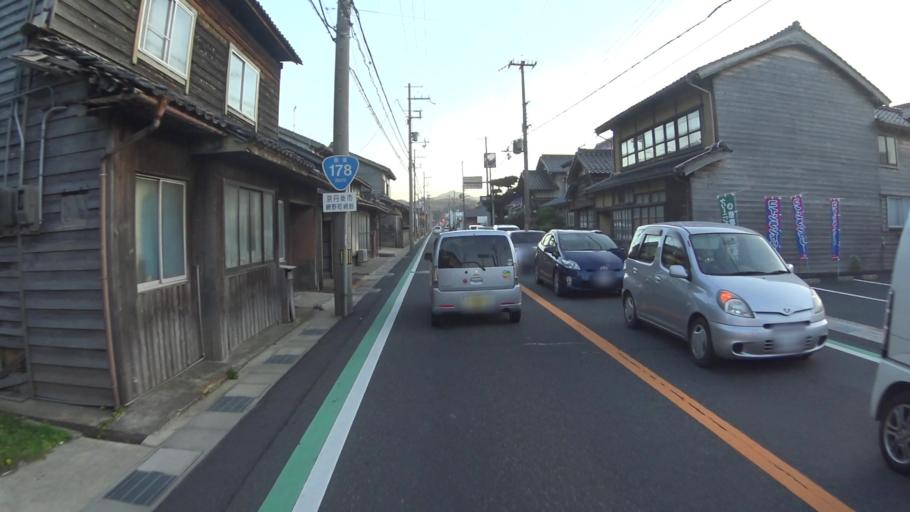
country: JP
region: Kyoto
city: Miyazu
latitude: 35.6776
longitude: 135.0284
